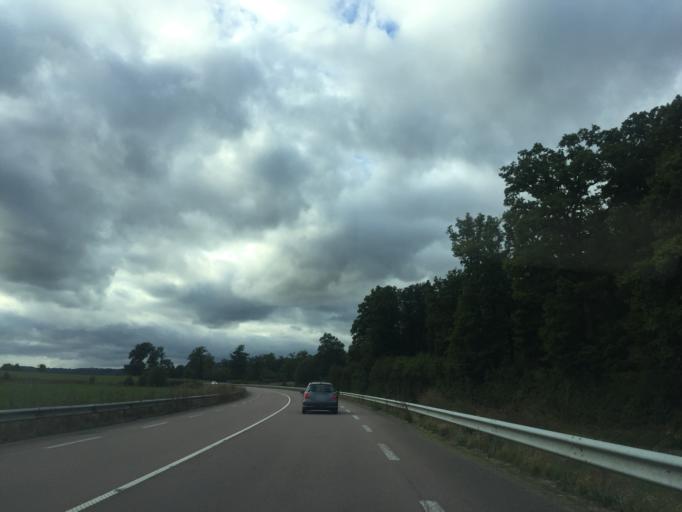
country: FR
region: Lorraine
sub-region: Departement des Vosges
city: Chatenois
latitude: 48.2989
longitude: 5.8799
